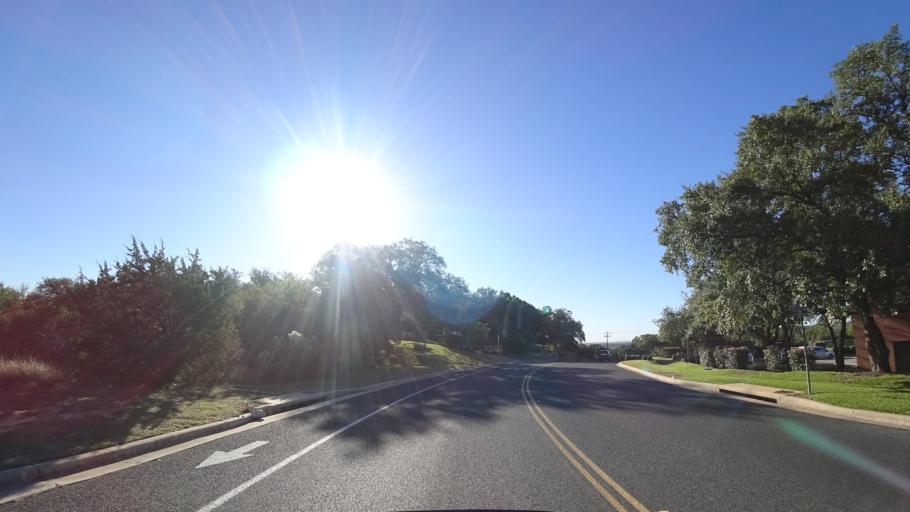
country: US
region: Texas
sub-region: Travis County
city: West Lake Hills
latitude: 30.3562
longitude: -97.7974
